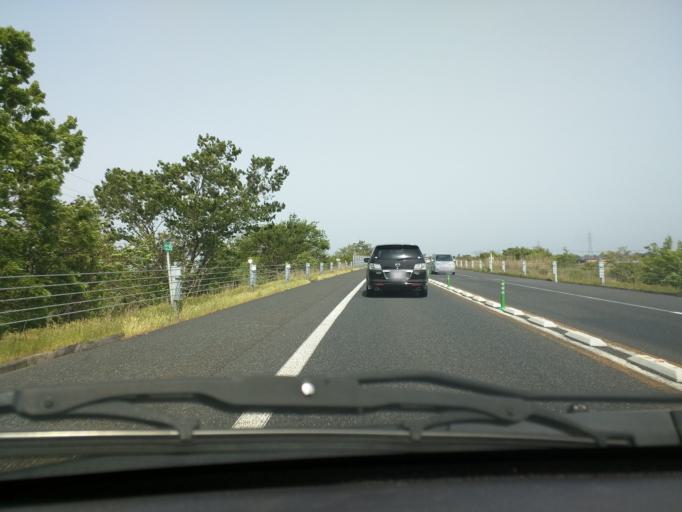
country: JP
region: Niigata
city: Niitsu-honcho
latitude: 37.7865
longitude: 139.1625
